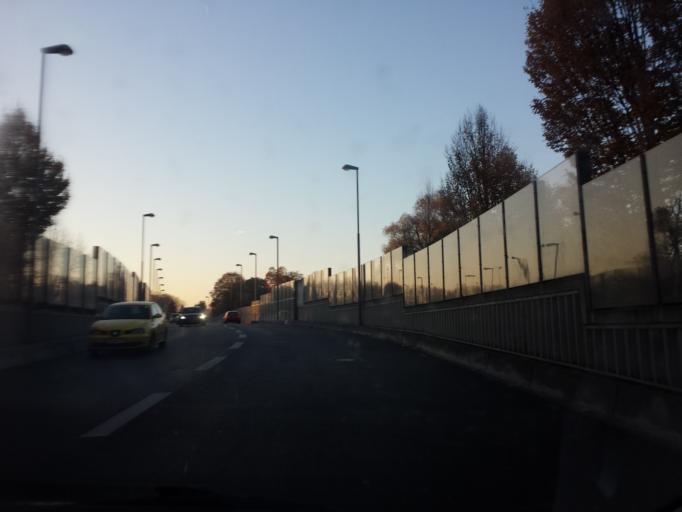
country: DE
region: Bavaria
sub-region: Upper Bavaria
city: Ingolstadt
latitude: 48.7562
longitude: 11.4261
